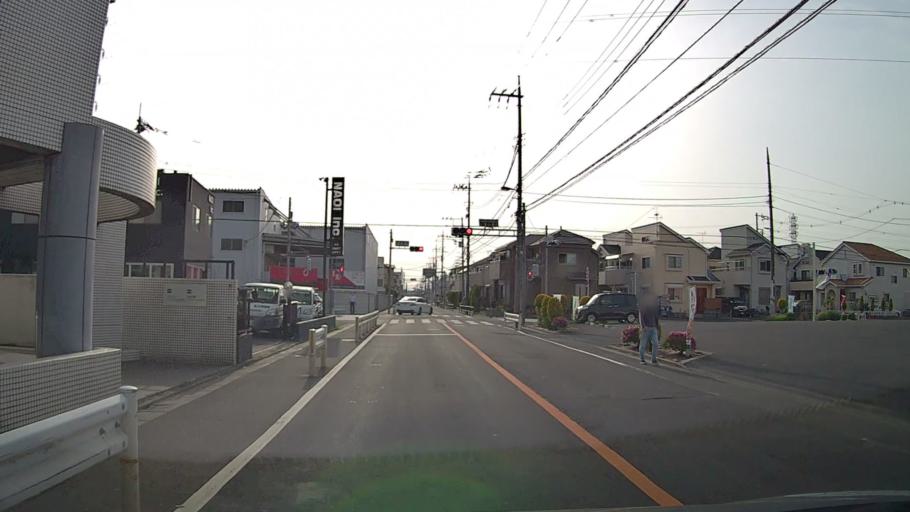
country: JP
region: Saitama
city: Soka
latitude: 35.8006
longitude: 139.7801
